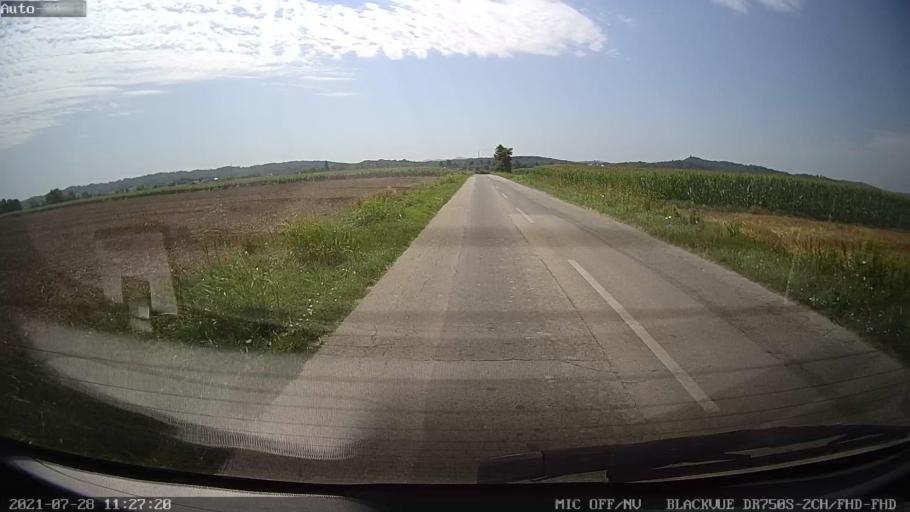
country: HR
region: Varazdinska
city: Jalzabet
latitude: 46.2664
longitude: 16.4348
